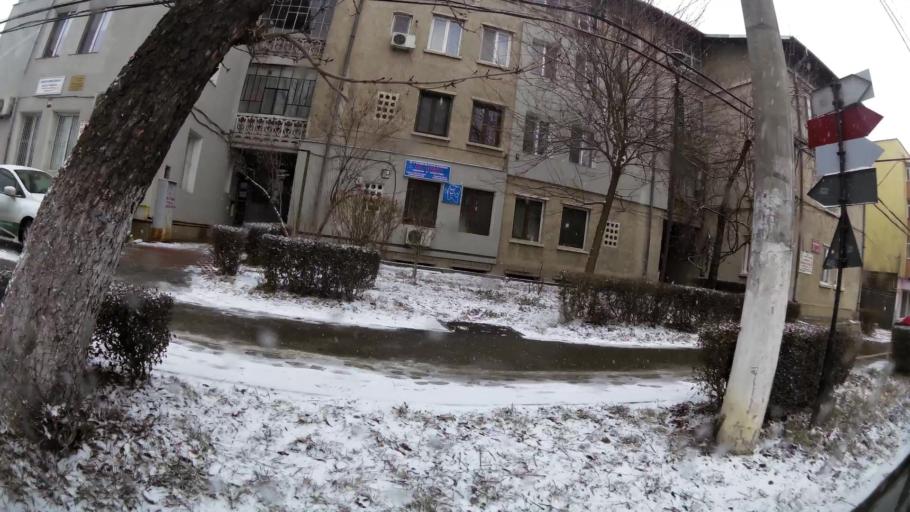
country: RO
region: Dambovita
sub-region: Municipiul Targoviste
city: Targoviste
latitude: 44.9208
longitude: 25.4558
